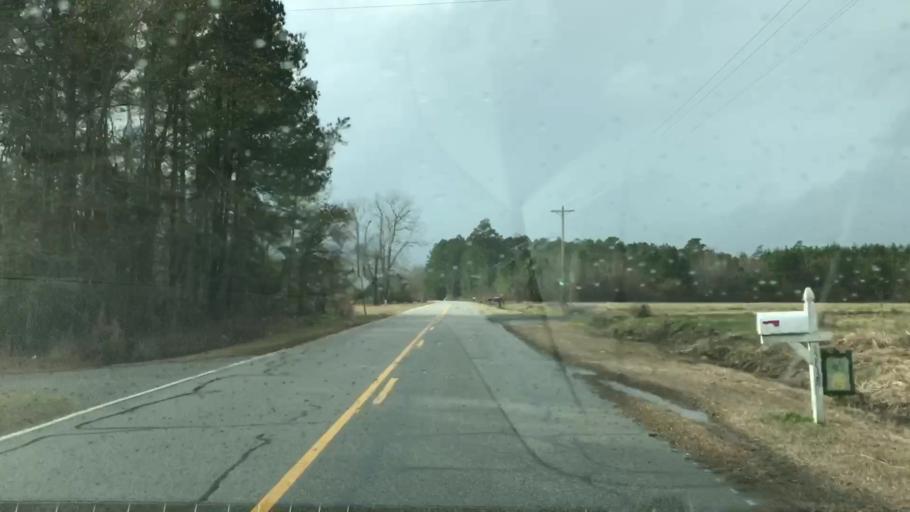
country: US
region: South Carolina
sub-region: Florence County
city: Johnsonville
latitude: 33.6778
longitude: -79.3853
